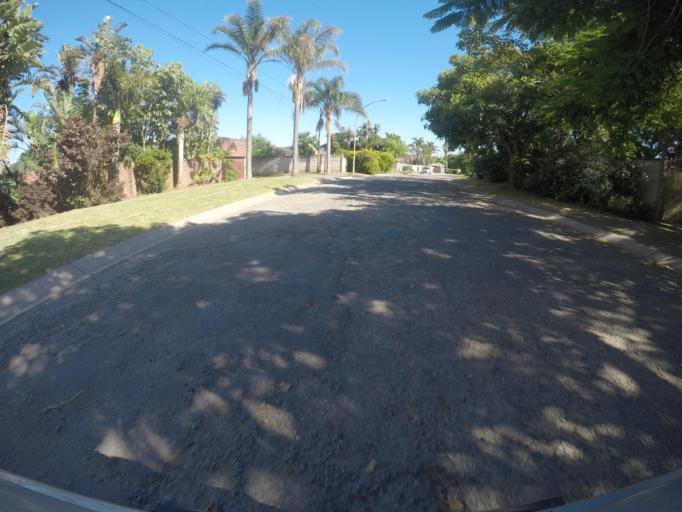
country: ZA
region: Eastern Cape
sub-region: Buffalo City Metropolitan Municipality
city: East London
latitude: -32.9502
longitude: 27.8977
